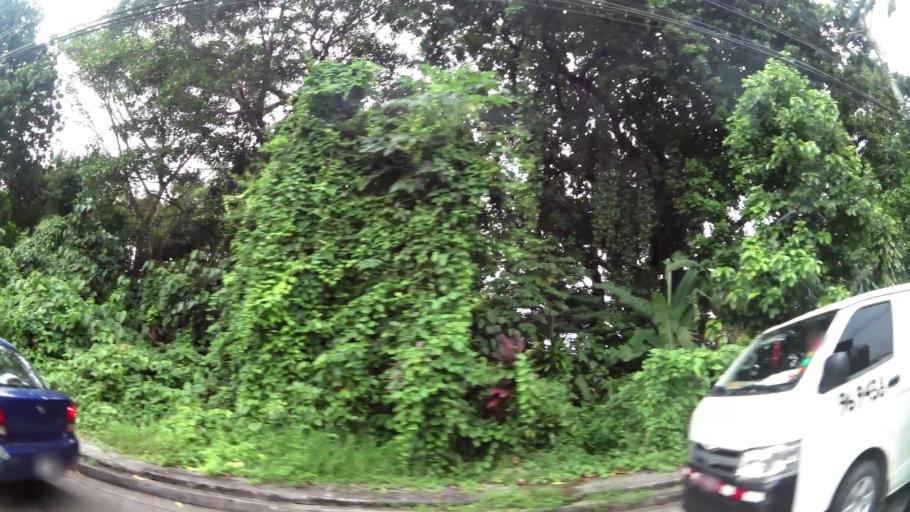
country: PA
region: Panama
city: Panama
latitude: 9.0121
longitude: -79.5407
